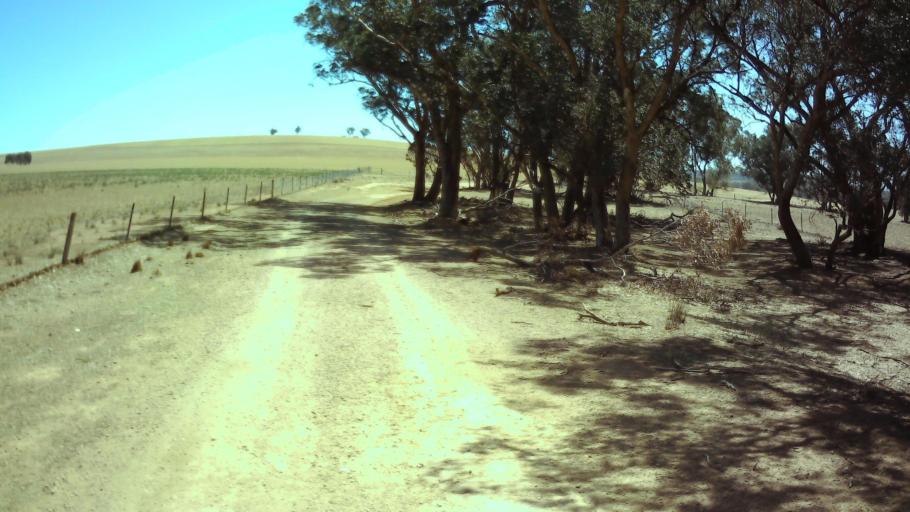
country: AU
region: New South Wales
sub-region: Weddin
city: Grenfell
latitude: -33.9819
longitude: 148.1655
